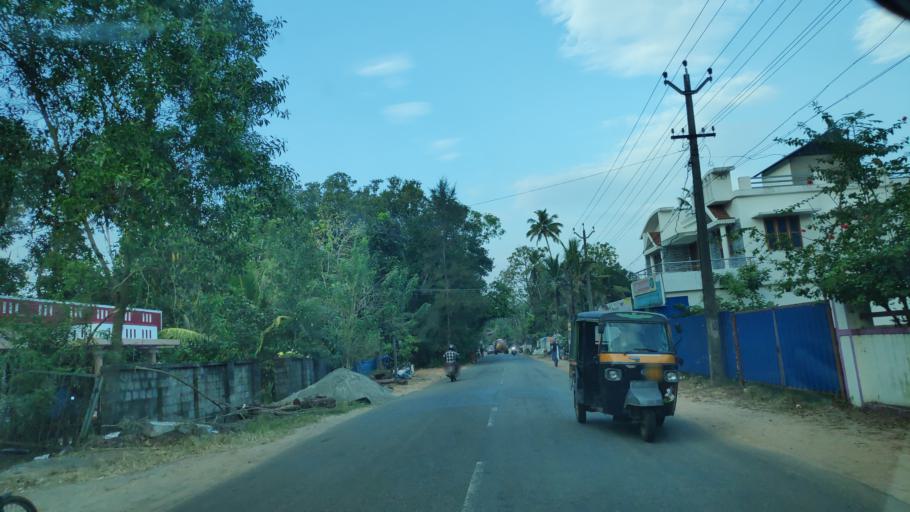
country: IN
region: Kerala
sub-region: Alappuzha
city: Shertallai
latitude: 9.6451
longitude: 76.3706
